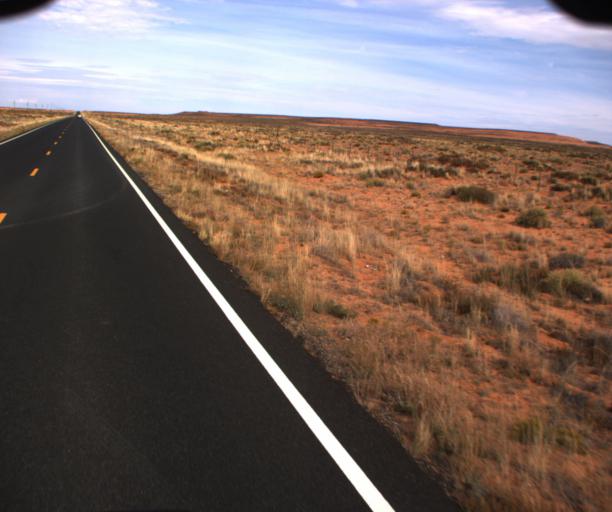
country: US
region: Arizona
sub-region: Apache County
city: Many Farms
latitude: 36.8411
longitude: -109.6414
